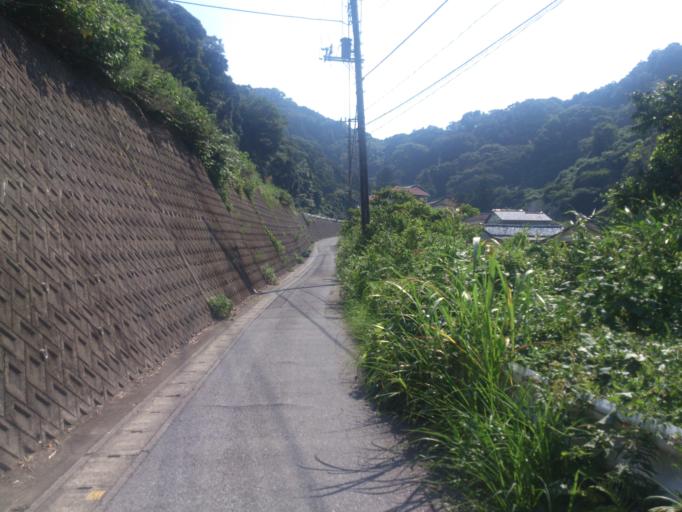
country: JP
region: Chiba
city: Tateyama
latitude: 35.0764
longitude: 139.8370
